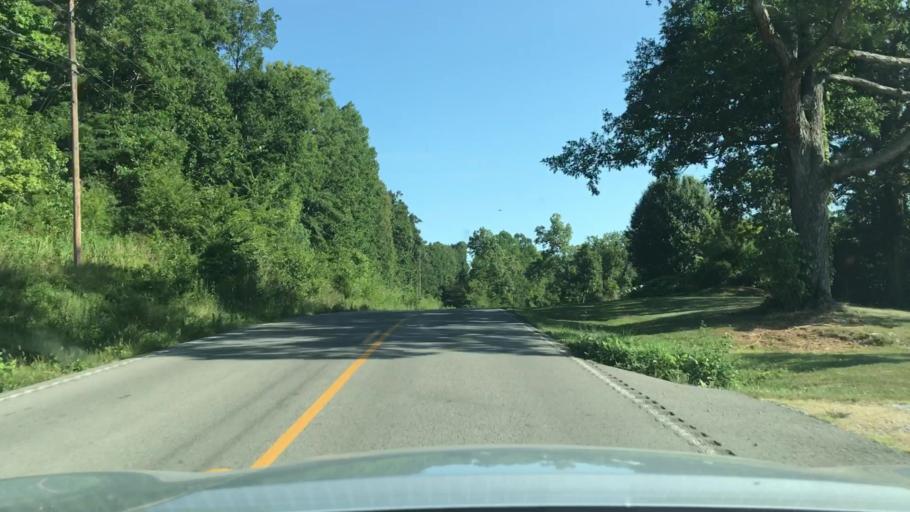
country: US
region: Kentucky
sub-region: Muhlenberg County
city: Greenville
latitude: 37.1081
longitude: -87.1276
